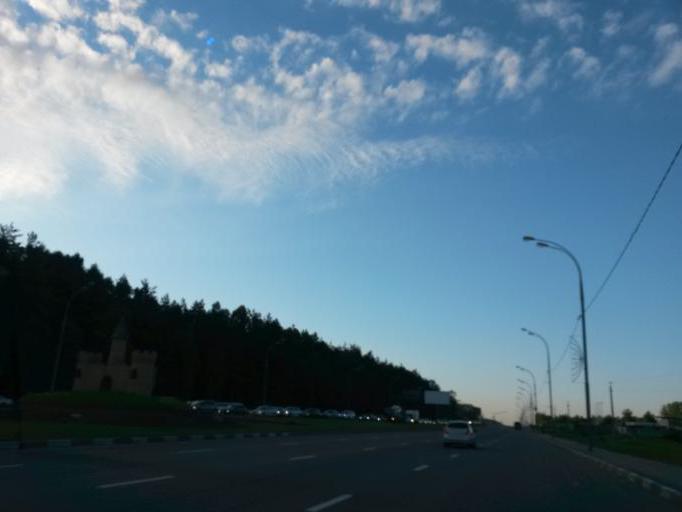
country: RU
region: Moscow
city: Annino
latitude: 55.5548
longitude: 37.5530
